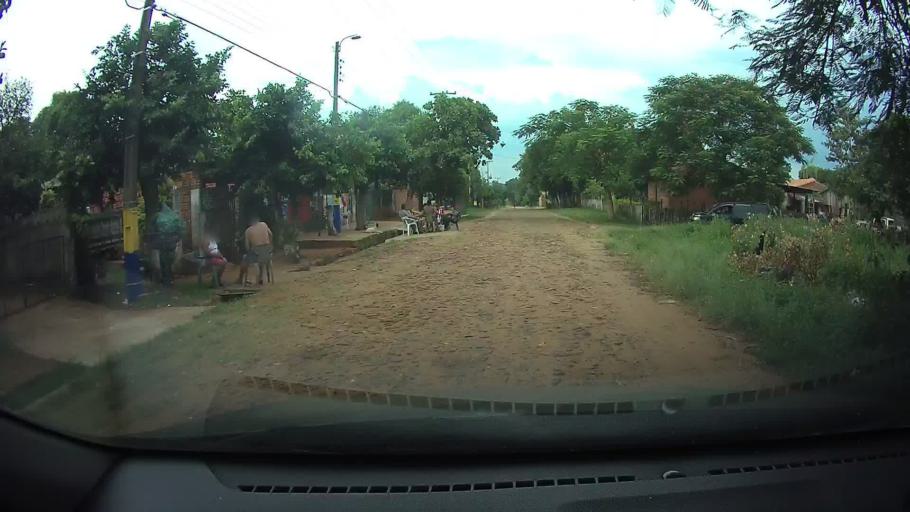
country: PY
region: Central
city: San Lorenzo
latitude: -25.2616
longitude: -57.4632
